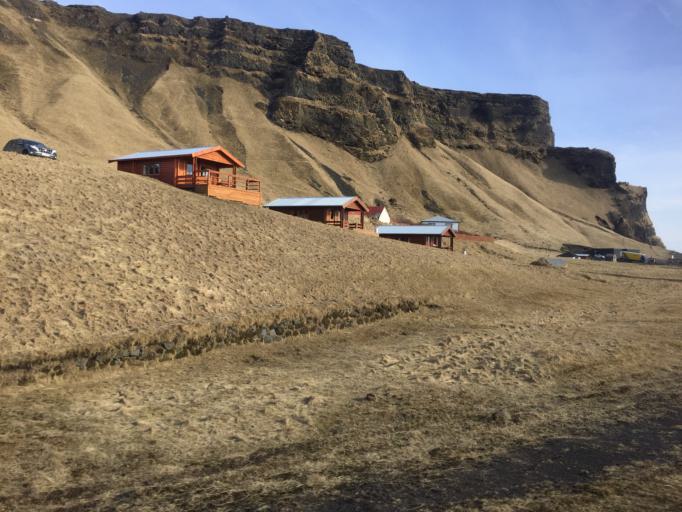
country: IS
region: South
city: Vestmannaeyjar
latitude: 63.4063
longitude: -19.0478
